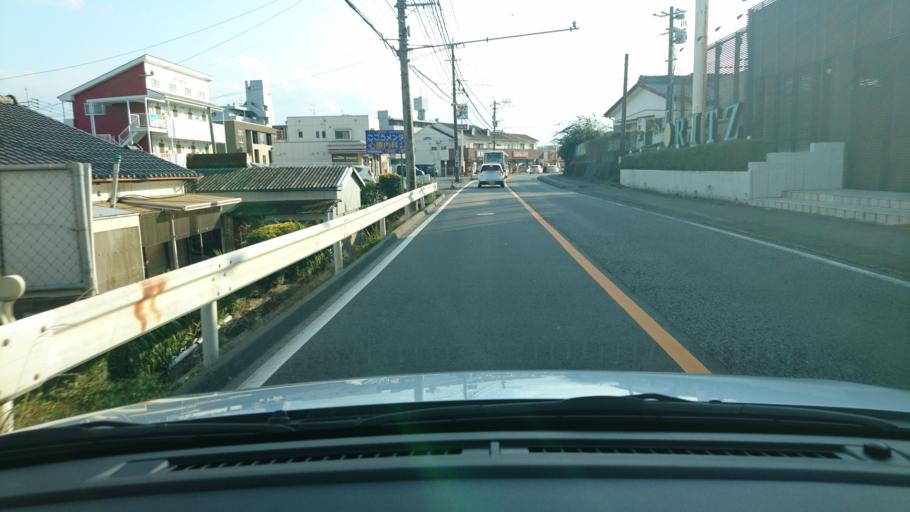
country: JP
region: Miyazaki
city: Miyazaki-shi
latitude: 31.8820
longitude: 131.4081
